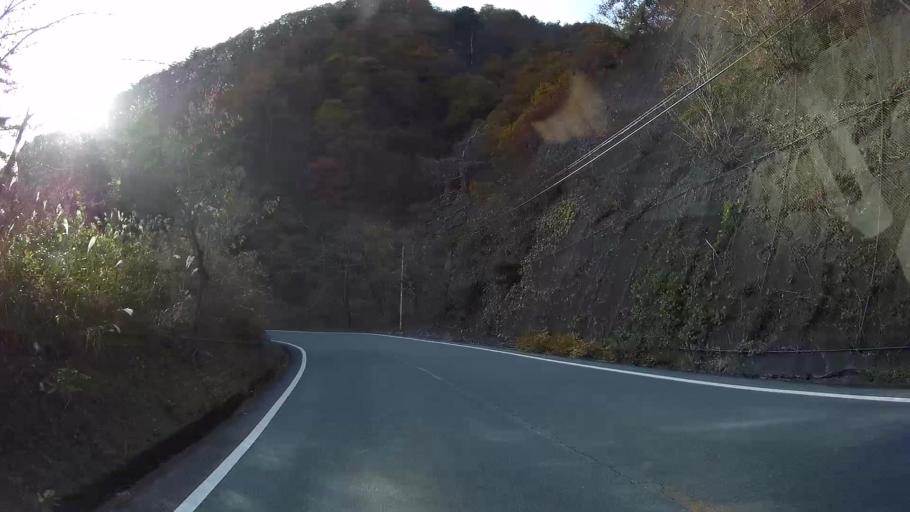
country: JP
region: Yamanashi
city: Fujikawaguchiko
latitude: 35.4822
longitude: 138.5566
